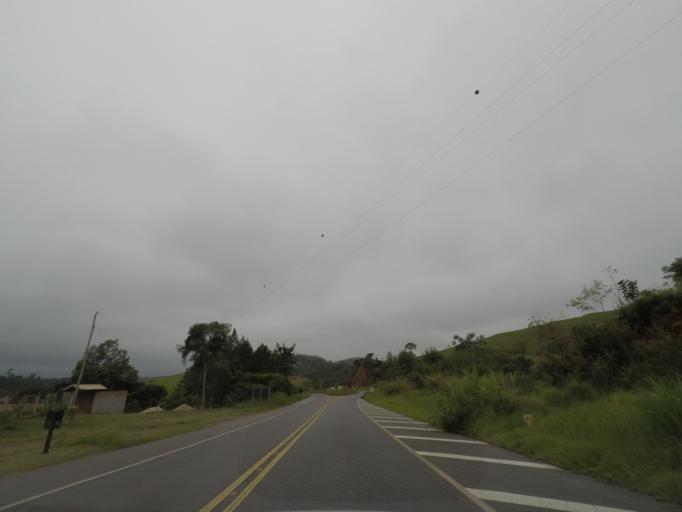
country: BR
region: Sao Paulo
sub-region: Guaratingueta
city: Guaratingueta
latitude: -22.9235
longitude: -45.0851
